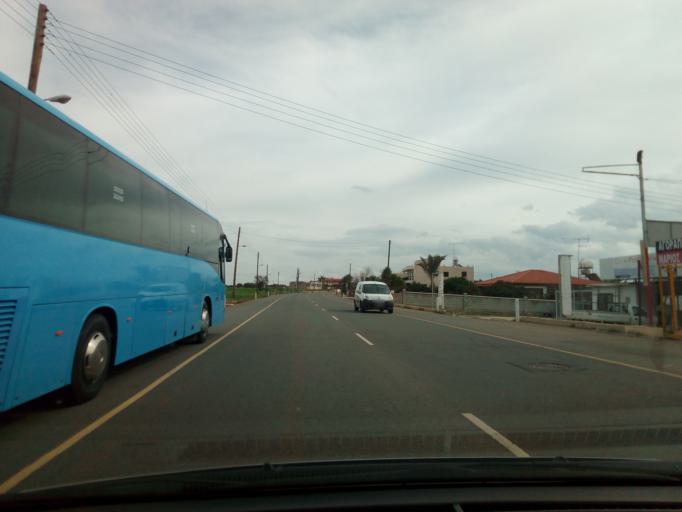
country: CY
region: Lefkosia
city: Peristerona
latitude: 35.1356
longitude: 33.0584
